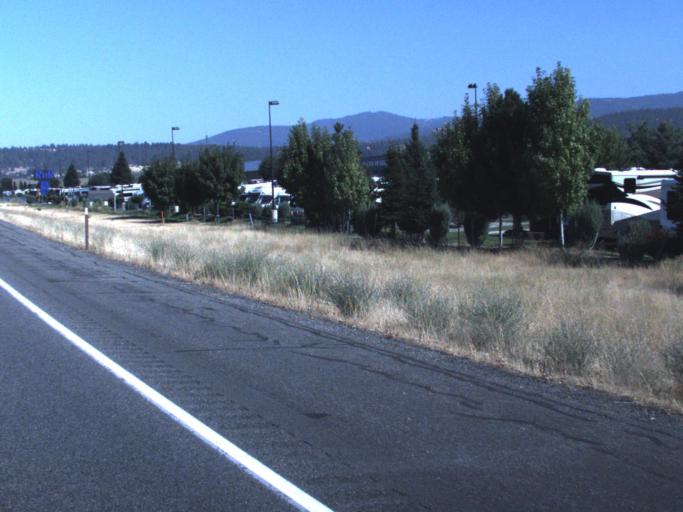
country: US
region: Washington
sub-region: Spokane County
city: Liberty Lake
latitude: 47.6791
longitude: -117.0982
